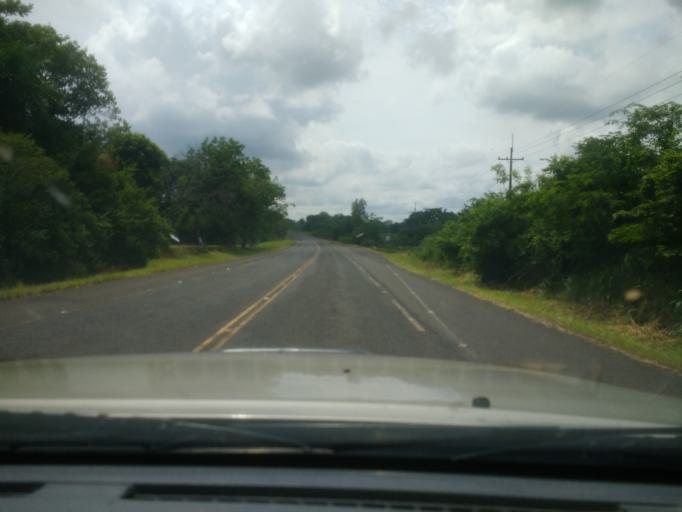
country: PY
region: San Pedro
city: Puerto Rosario
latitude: -24.4342
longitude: -57.0375
